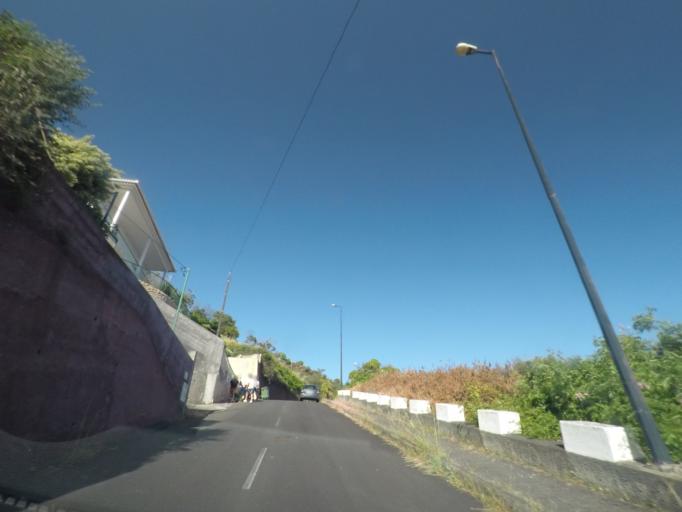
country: PT
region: Madeira
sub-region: Santa Cruz
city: Santa Cruz
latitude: 32.6926
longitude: -16.7980
